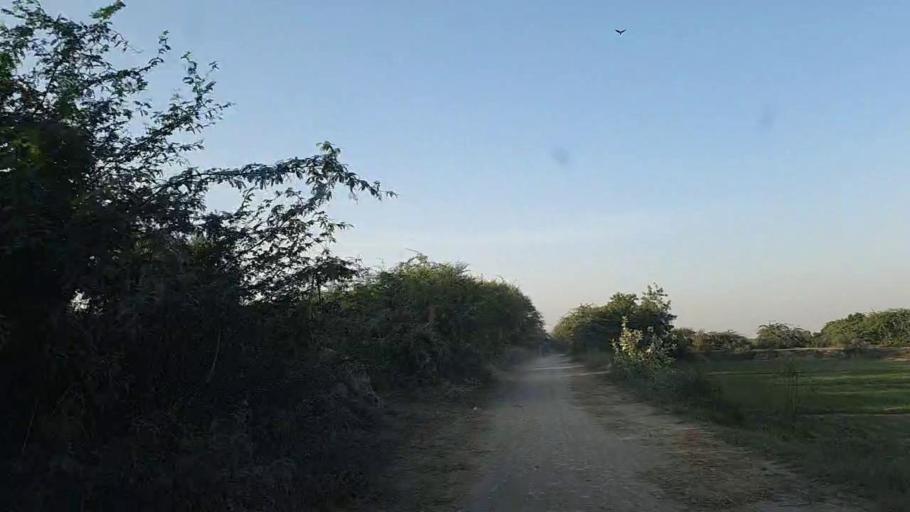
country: PK
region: Sindh
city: Mirpur Batoro
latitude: 24.7183
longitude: 68.2142
